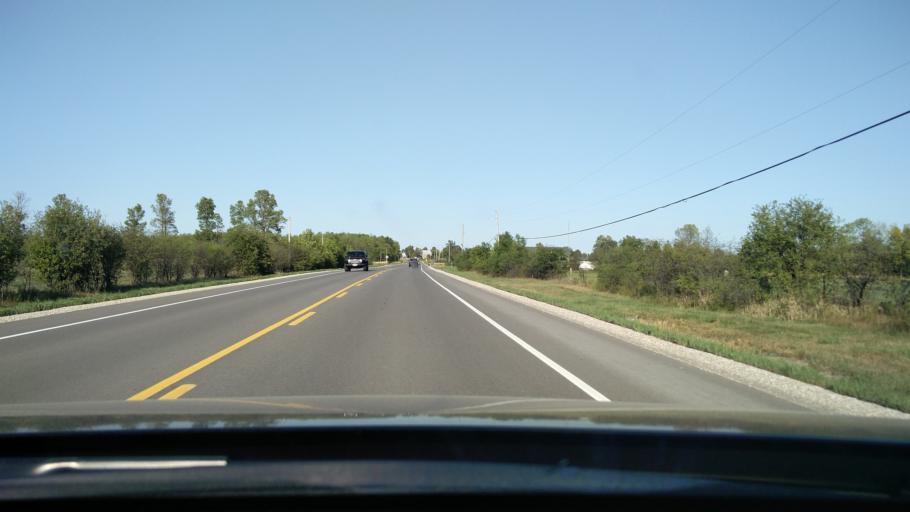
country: CA
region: Ontario
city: Perth
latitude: 44.9450
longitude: -76.1805
